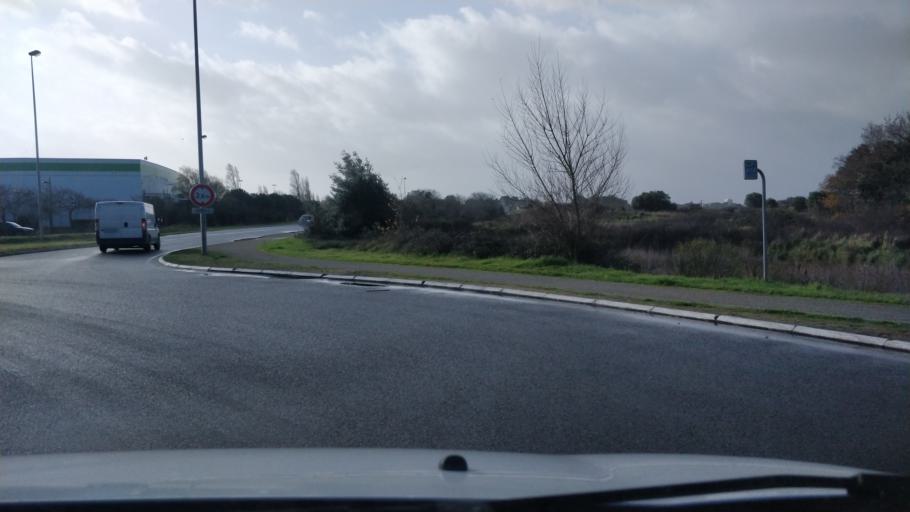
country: FR
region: Pays de la Loire
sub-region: Departement de la Loire-Atlantique
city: La Baule-Escoublac
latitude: 47.2944
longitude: -2.3983
